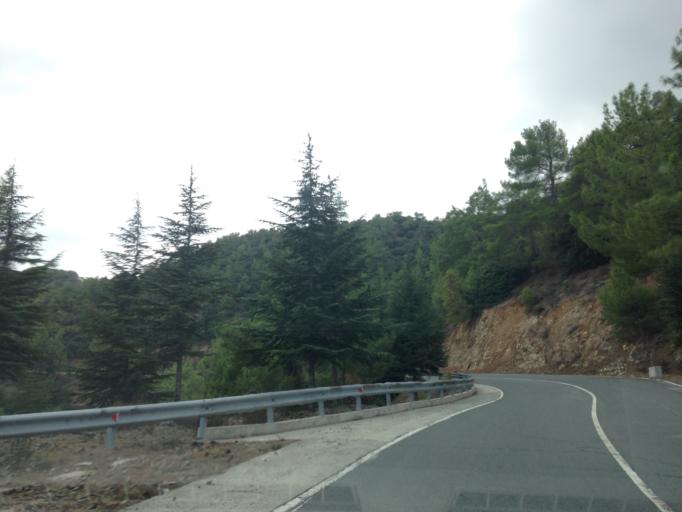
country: CY
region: Lefkosia
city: Lefka
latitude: 35.0002
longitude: 32.7355
